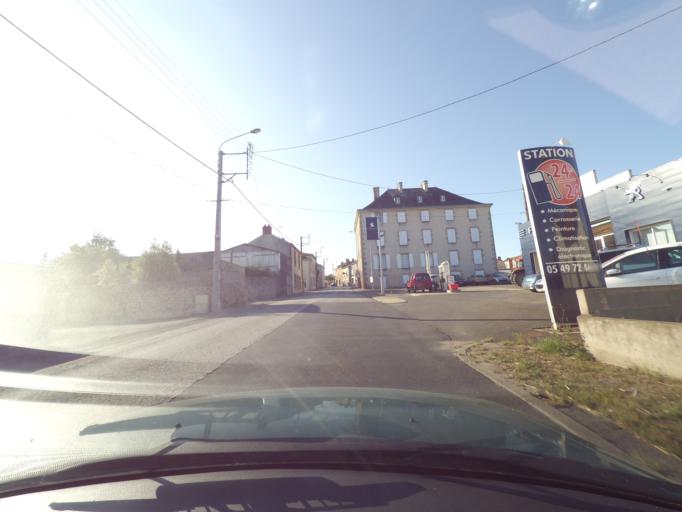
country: FR
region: Poitou-Charentes
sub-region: Departement des Deux-Sevres
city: Chiche
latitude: 46.7979
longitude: -0.3606
